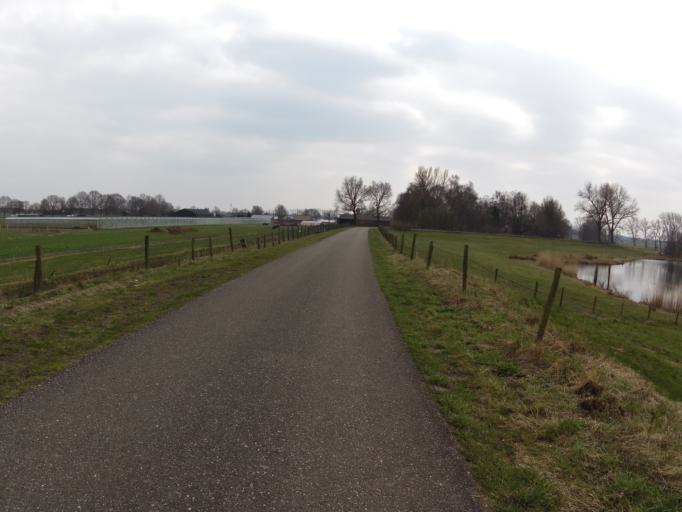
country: NL
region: North Brabant
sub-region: Gemeente Heusden
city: Heusden
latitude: 51.7014
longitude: 5.1150
